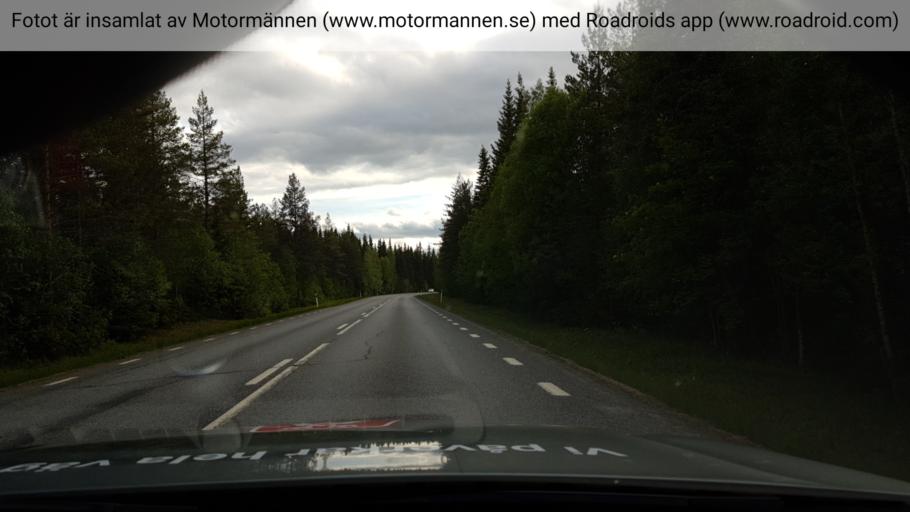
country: SE
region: Jaemtland
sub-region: Stroemsunds Kommun
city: Stroemsund
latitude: 63.5253
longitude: 15.3206
